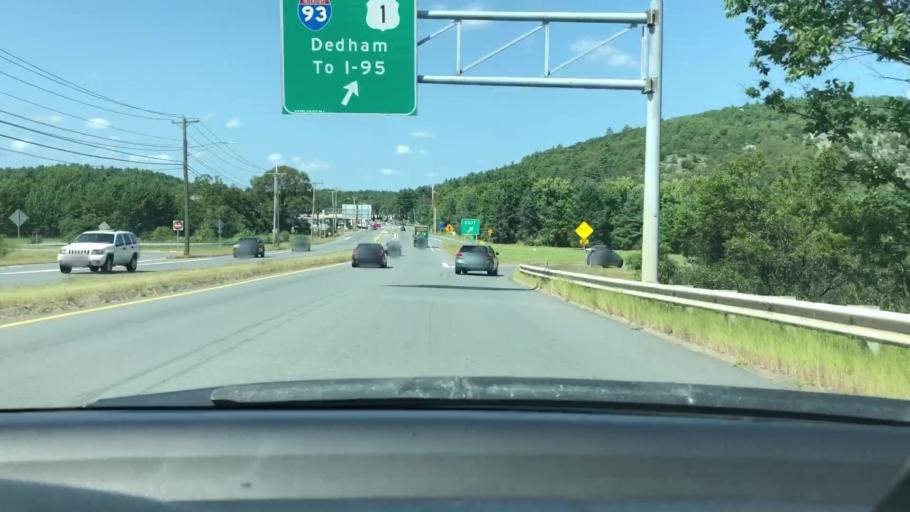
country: US
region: Massachusetts
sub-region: Norfolk County
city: Canton
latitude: 42.2039
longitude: -71.1192
